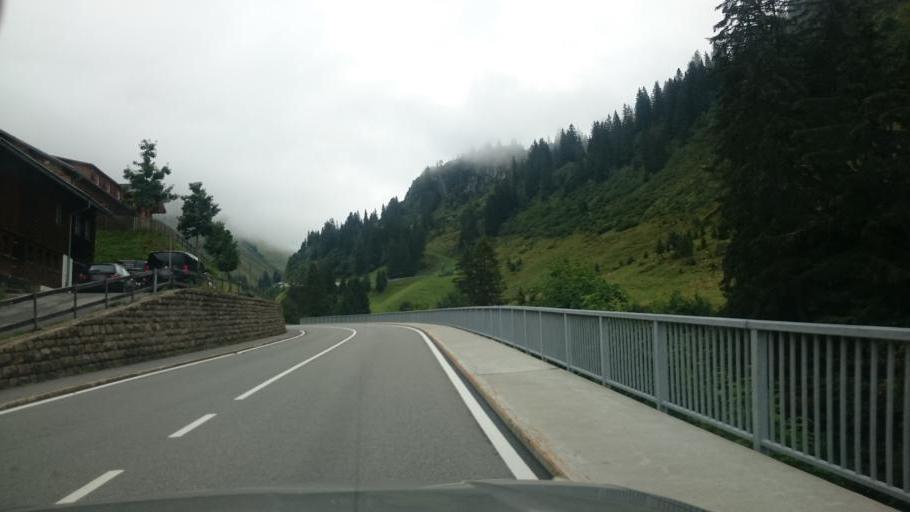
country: AT
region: Vorarlberg
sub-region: Politischer Bezirk Bregenz
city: Schroecken
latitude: 47.2622
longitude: 10.1035
